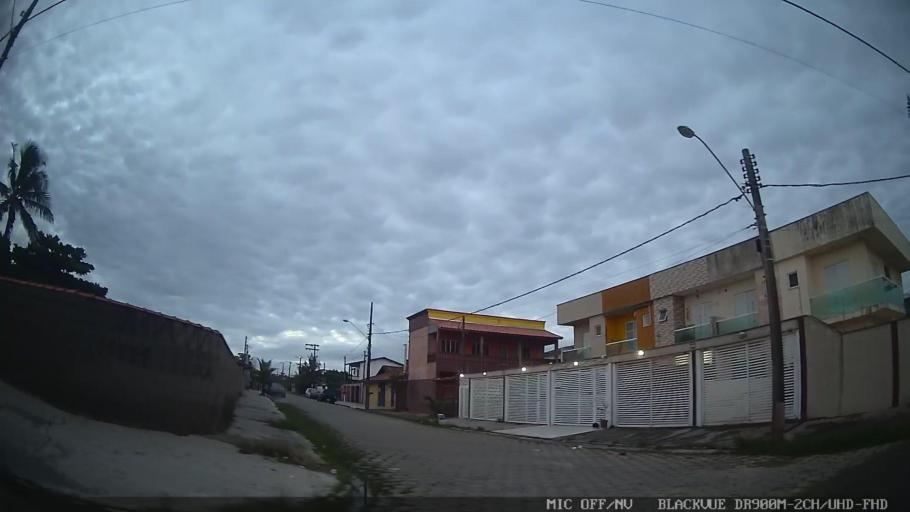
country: BR
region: Sao Paulo
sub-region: Itanhaem
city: Itanhaem
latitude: -24.2301
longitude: -46.8661
